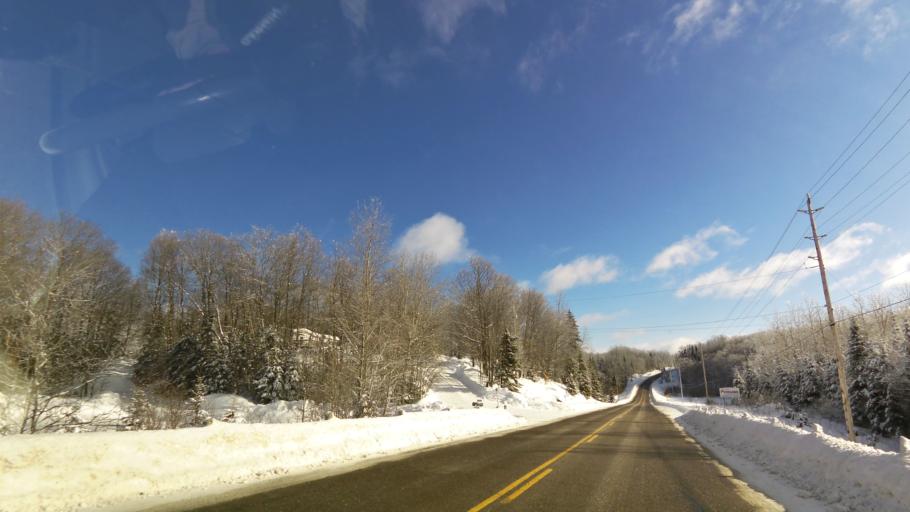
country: CA
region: Ontario
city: Bancroft
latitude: 45.0110
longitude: -78.3166
